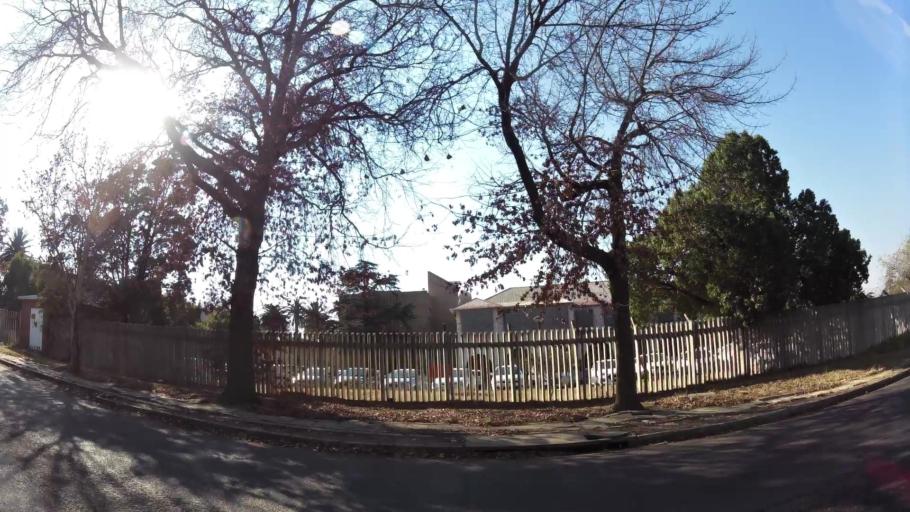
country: ZA
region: Gauteng
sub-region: Ekurhuleni Metropolitan Municipality
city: Boksburg
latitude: -26.2176
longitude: 28.2435
